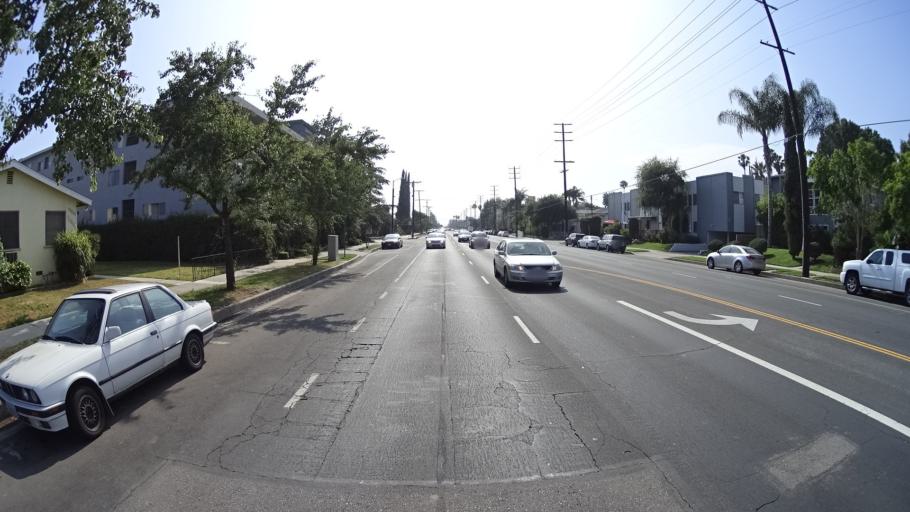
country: US
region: California
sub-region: Los Angeles County
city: Van Nuys
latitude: 34.1722
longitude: -118.4349
